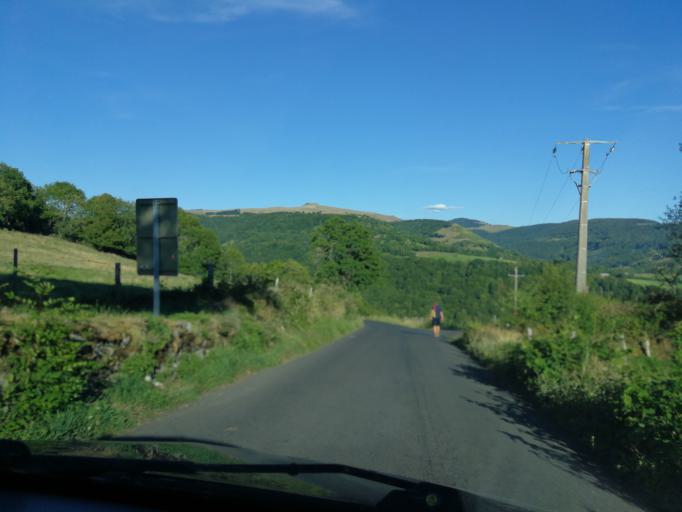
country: FR
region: Auvergne
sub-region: Departement du Cantal
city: Saint-Cernin
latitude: 45.1381
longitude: 2.4970
